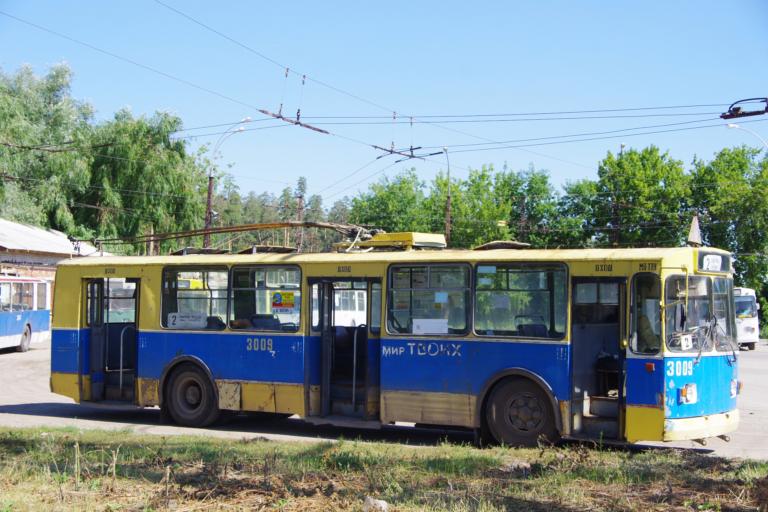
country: RU
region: Samara
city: Tol'yatti
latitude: 53.5049
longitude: 49.3897
